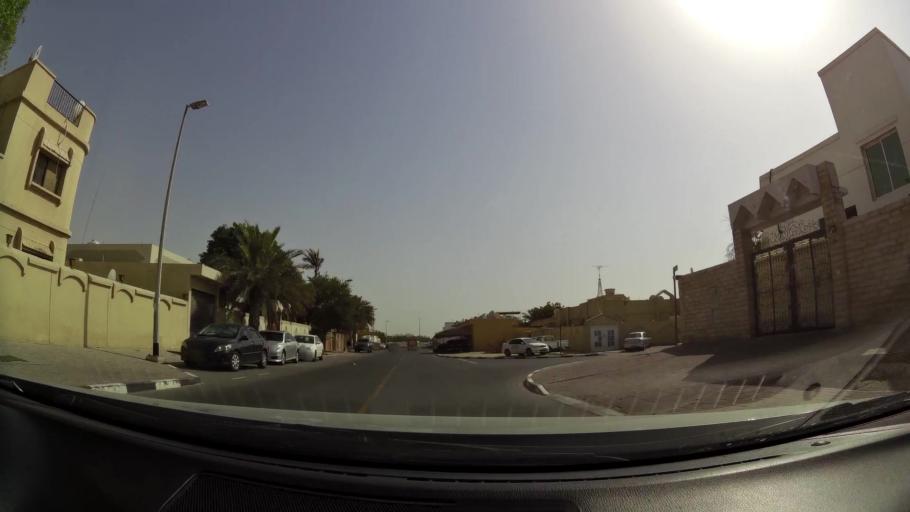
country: AE
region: Dubai
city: Dubai
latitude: 25.1683
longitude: 55.2443
